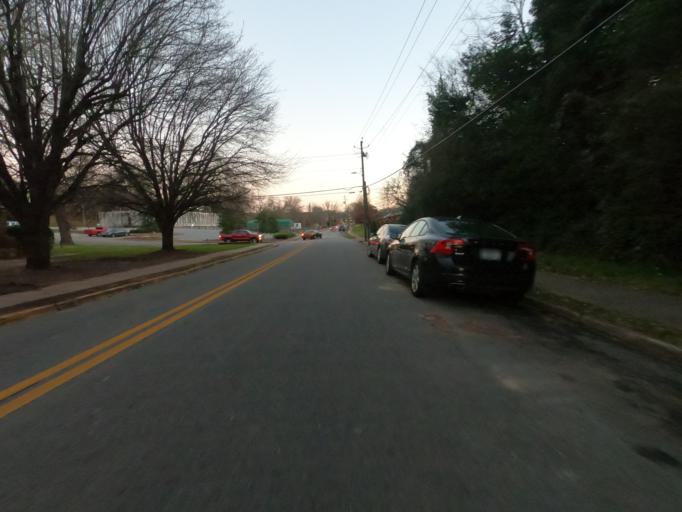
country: US
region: Georgia
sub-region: Clarke County
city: Athens
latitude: 33.9543
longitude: -83.3806
